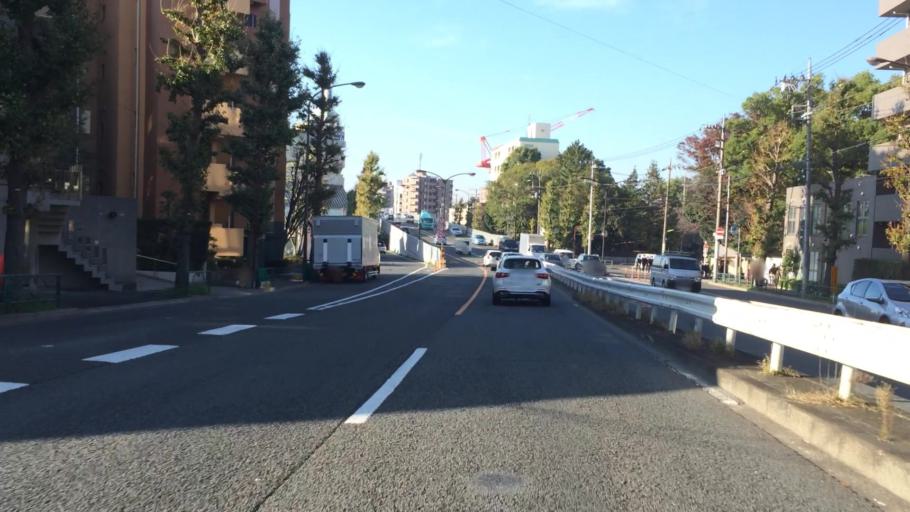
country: JP
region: Tokyo
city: Tokyo
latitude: 35.6102
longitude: 139.6512
